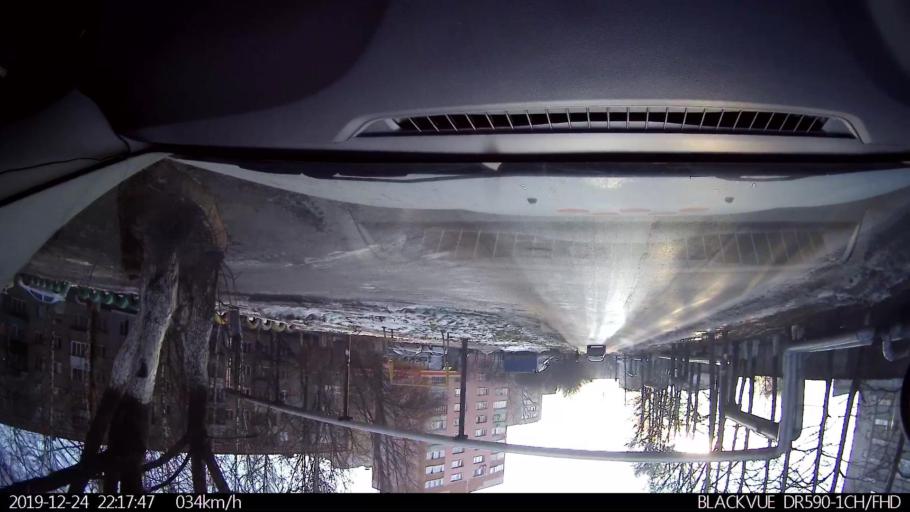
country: RU
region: Nizjnij Novgorod
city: Nizhniy Novgorod
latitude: 56.2404
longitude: 43.9720
